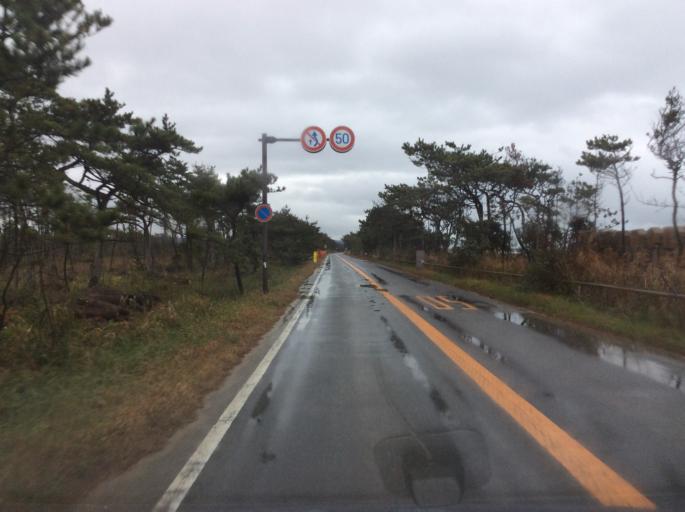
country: JP
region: Fukushima
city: Iwaki
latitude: 37.0676
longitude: 140.9761
